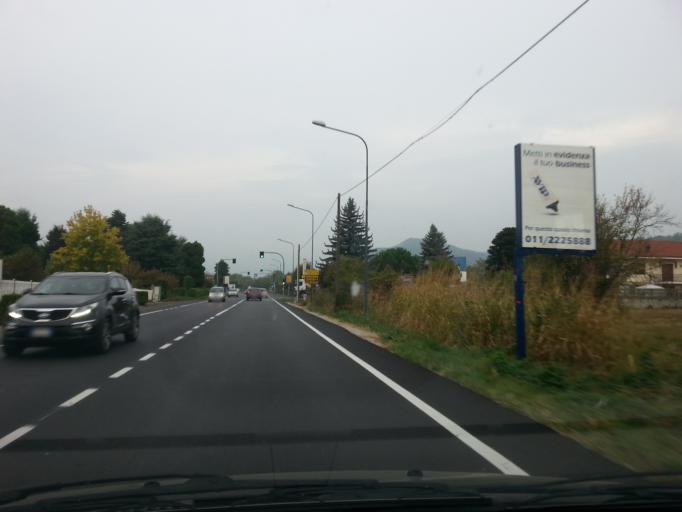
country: IT
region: Piedmont
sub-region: Provincia di Torino
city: Sangano
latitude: 45.0320
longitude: 7.4377
